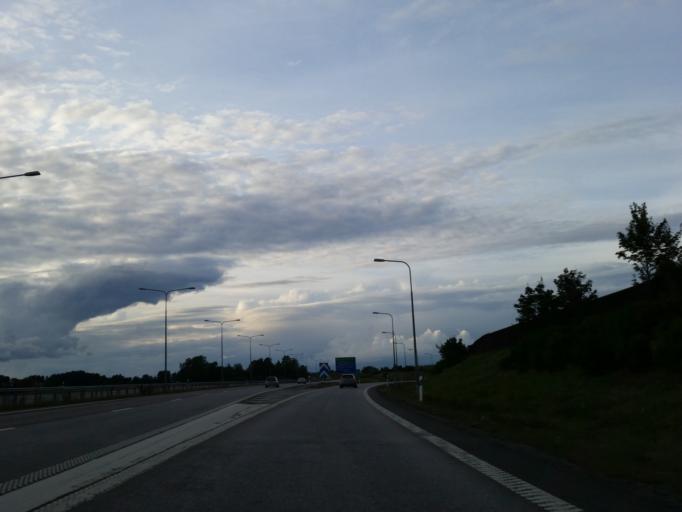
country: SE
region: Uppsala
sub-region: Uppsala Kommun
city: Saevja
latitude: 59.8303
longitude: 17.7369
